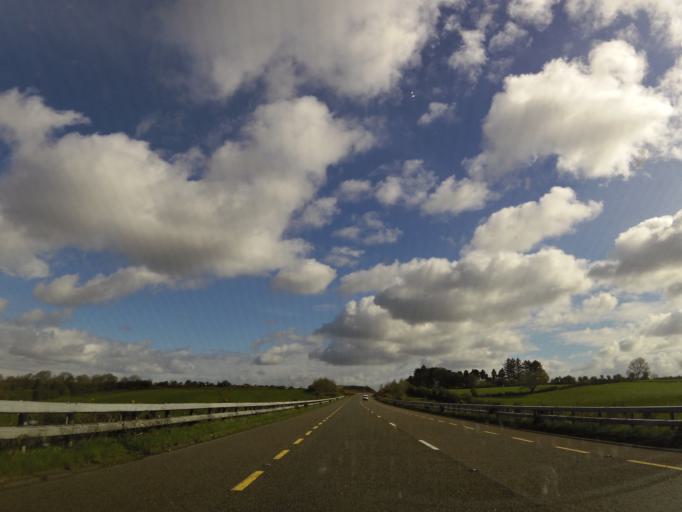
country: IE
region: Connaught
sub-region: Maigh Eo
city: Claremorris
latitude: 53.7815
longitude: -8.9454
